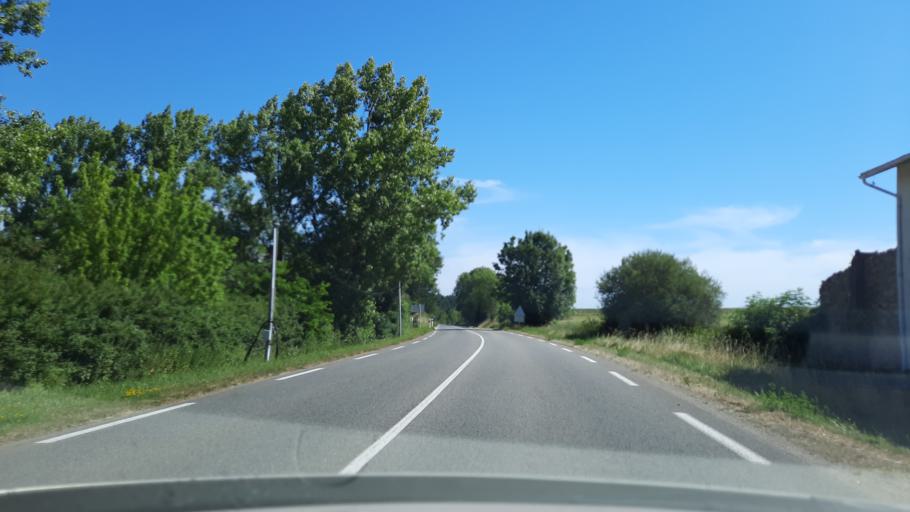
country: FR
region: Midi-Pyrenees
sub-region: Departement de l'Aveyron
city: Montbazens
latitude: 44.4518
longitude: 2.2150
